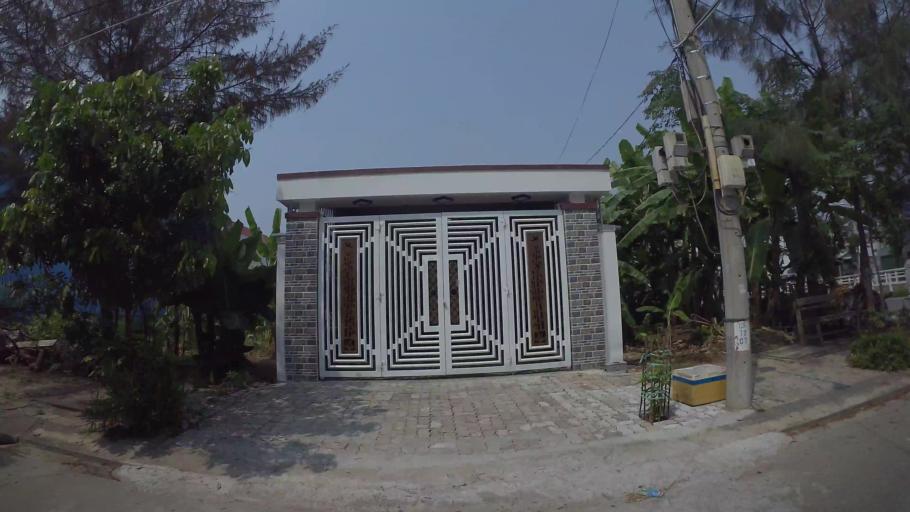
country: VN
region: Da Nang
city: Cam Le
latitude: 15.9824
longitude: 108.2092
